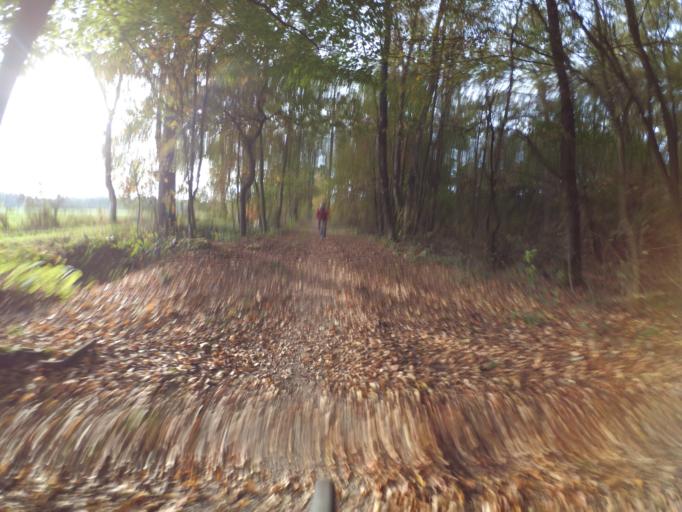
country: NL
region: Gelderland
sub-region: Gemeente Lochem
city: Harfsen
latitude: 52.2725
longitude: 6.3085
